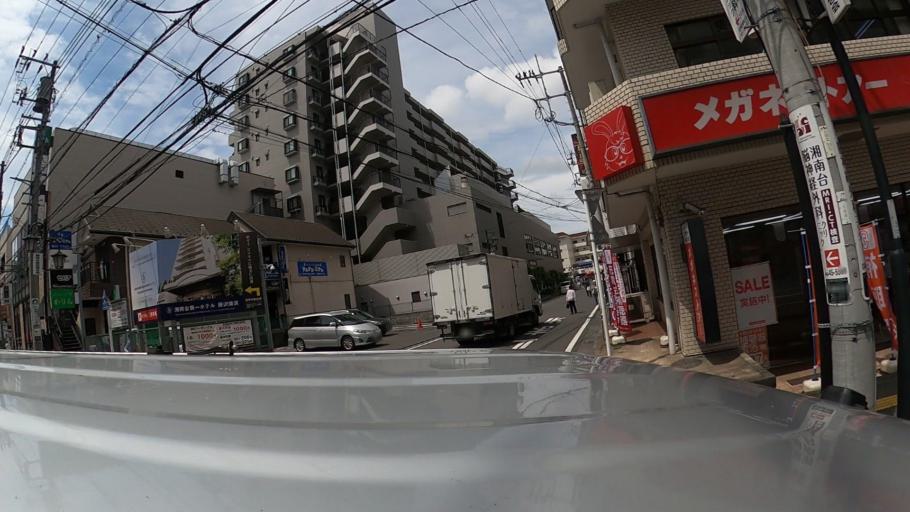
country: JP
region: Kanagawa
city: Fujisawa
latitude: 35.3971
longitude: 139.4648
